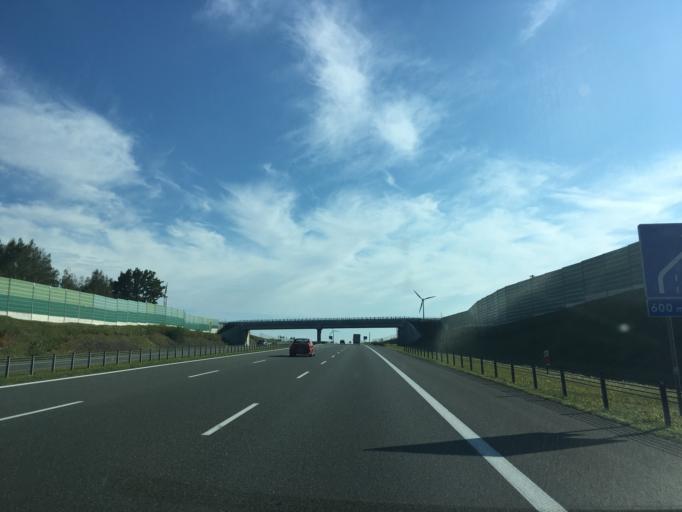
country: PL
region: Kujawsko-Pomorskie
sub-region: Powiat chelminski
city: Lisewo
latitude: 53.3845
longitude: 18.6872
